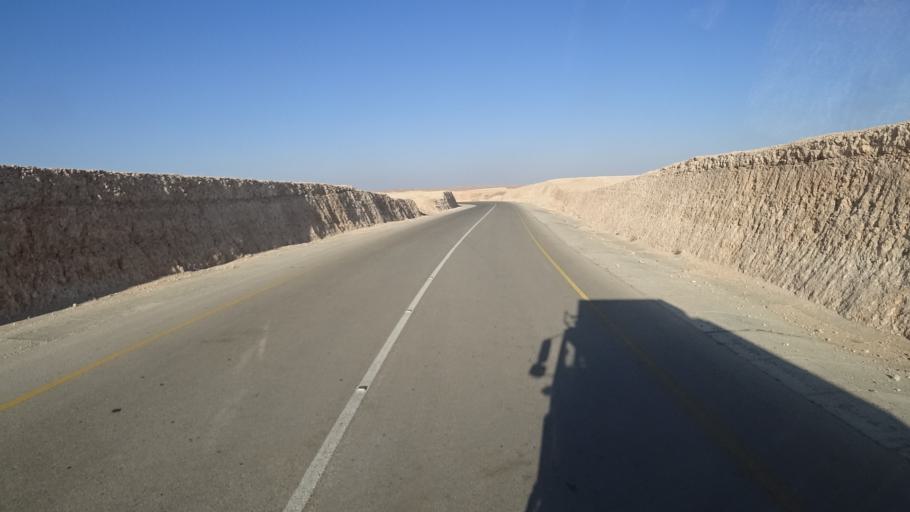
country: YE
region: Al Mahrah
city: Hawf
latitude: 17.0881
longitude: 53.0350
